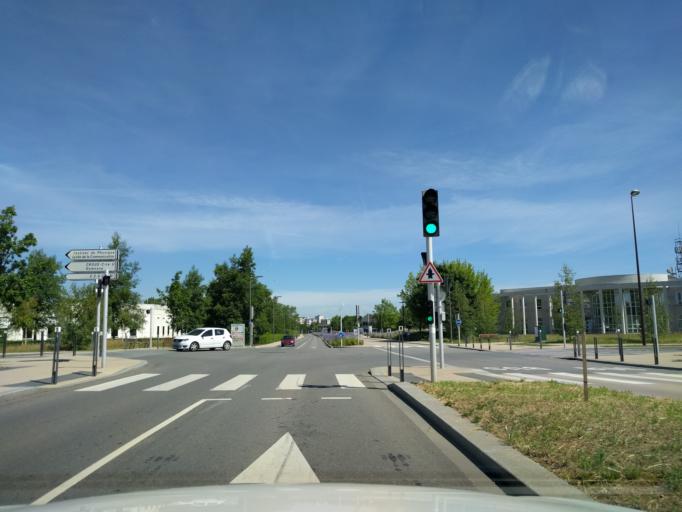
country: FR
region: Lorraine
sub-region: Departement de la Moselle
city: Peltre
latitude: 49.1004
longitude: 6.2243
